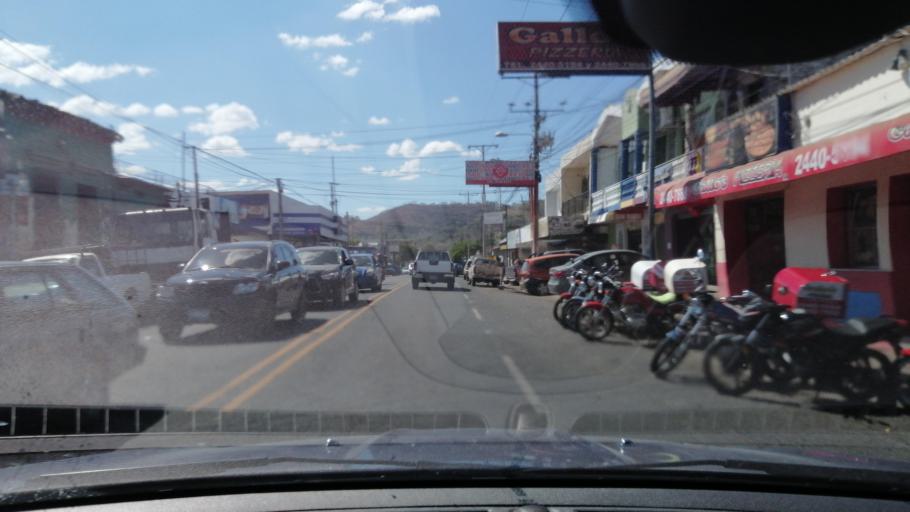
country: SV
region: Santa Ana
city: Santa Ana
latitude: 13.9827
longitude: -89.5609
